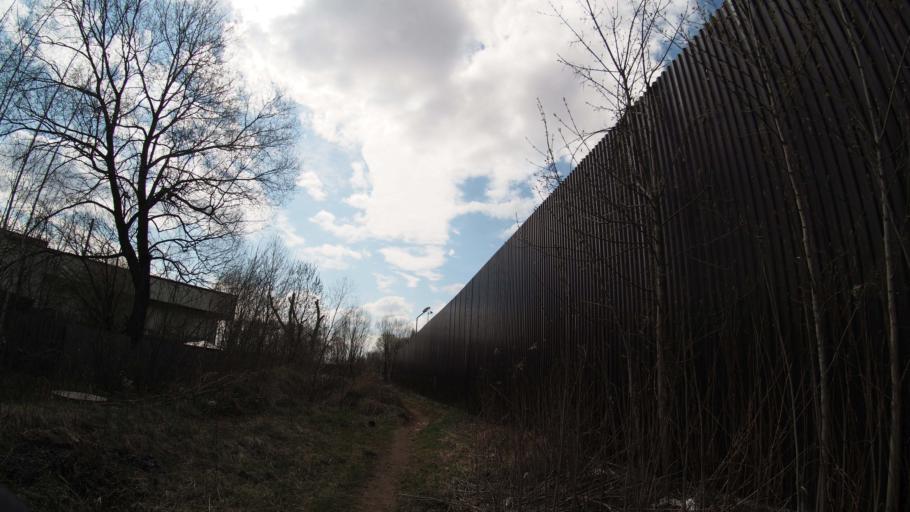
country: RU
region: Moskovskaya
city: Ramenskoye
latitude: 55.5620
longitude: 38.2270
